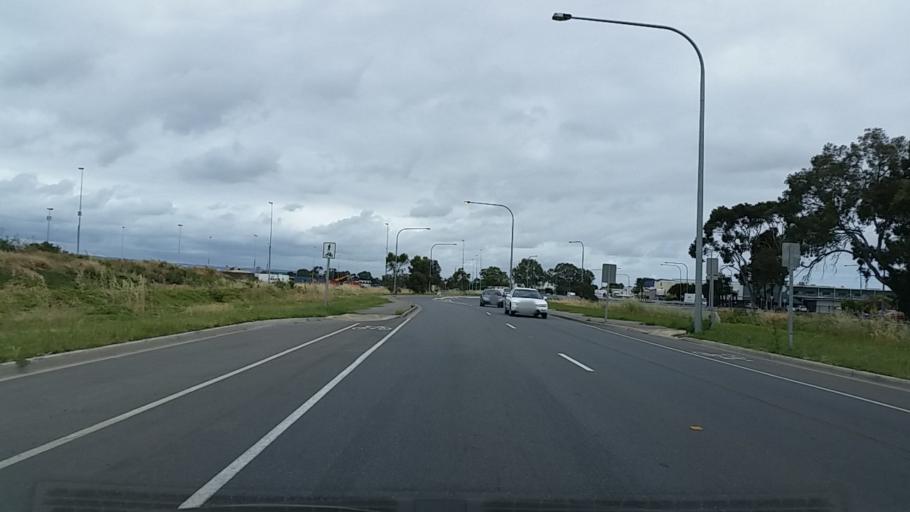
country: AU
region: South Australia
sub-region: Port Adelaide Enfield
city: Blair Athol
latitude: -34.8612
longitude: 138.5748
